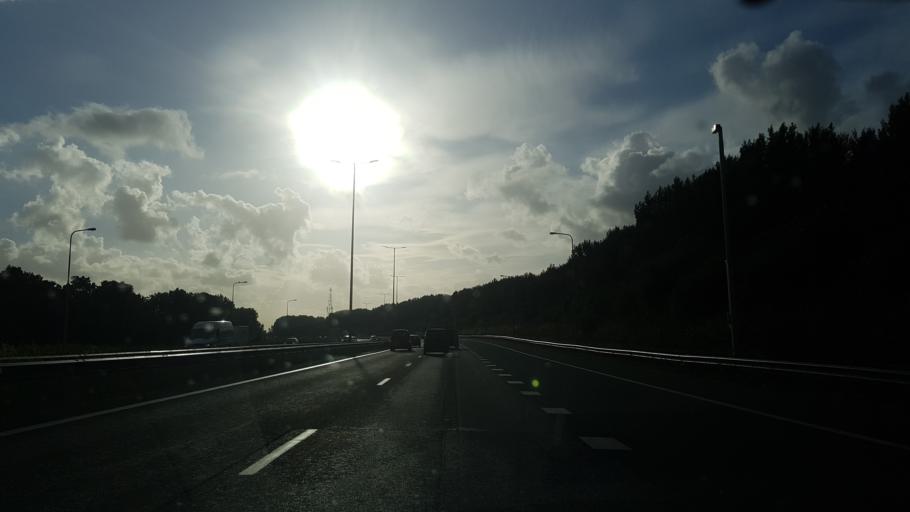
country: NL
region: Groningen
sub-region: Gemeente Groningen
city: Groningen
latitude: 53.2023
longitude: 6.5033
